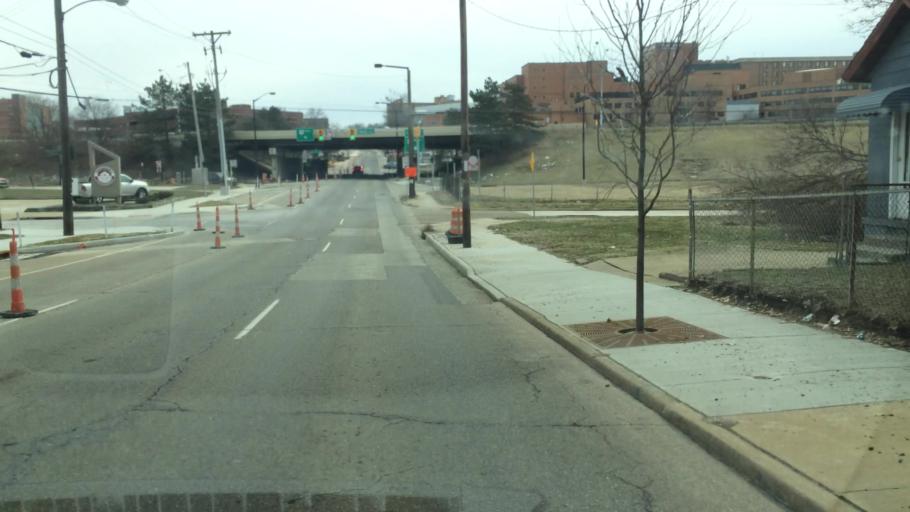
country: US
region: Ohio
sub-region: Summit County
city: Akron
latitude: 41.0811
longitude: -81.5334
